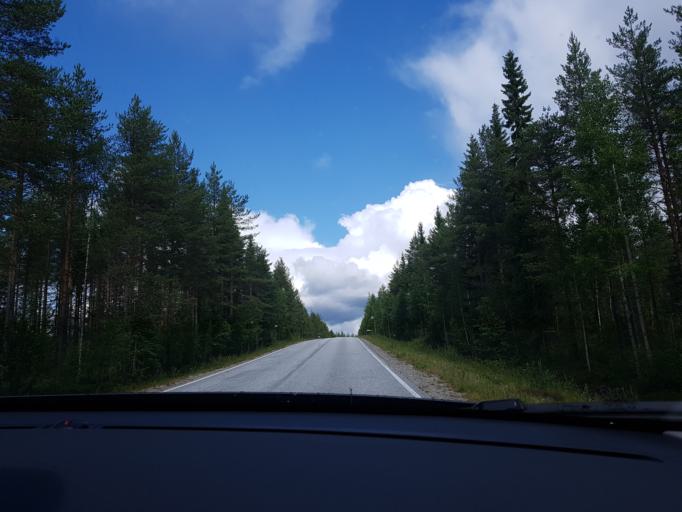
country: FI
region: Kainuu
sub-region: Kehys-Kainuu
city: Kuhmo
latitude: 64.4309
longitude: 29.4965
